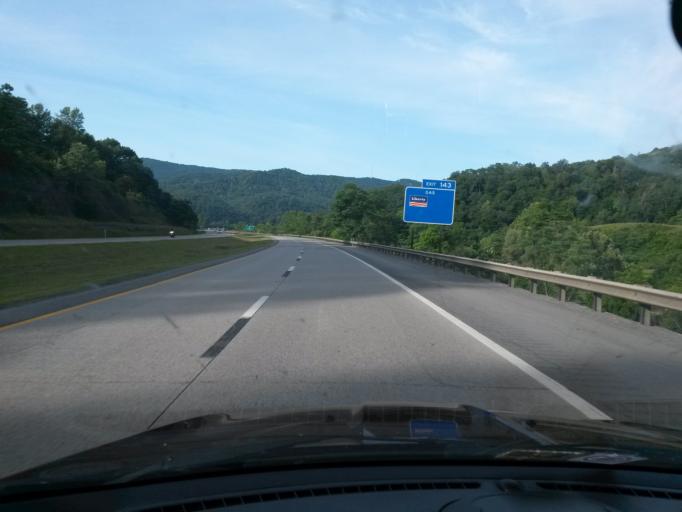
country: US
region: West Virginia
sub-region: Greenbrier County
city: Rainelle
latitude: 37.8201
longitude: -80.8123
